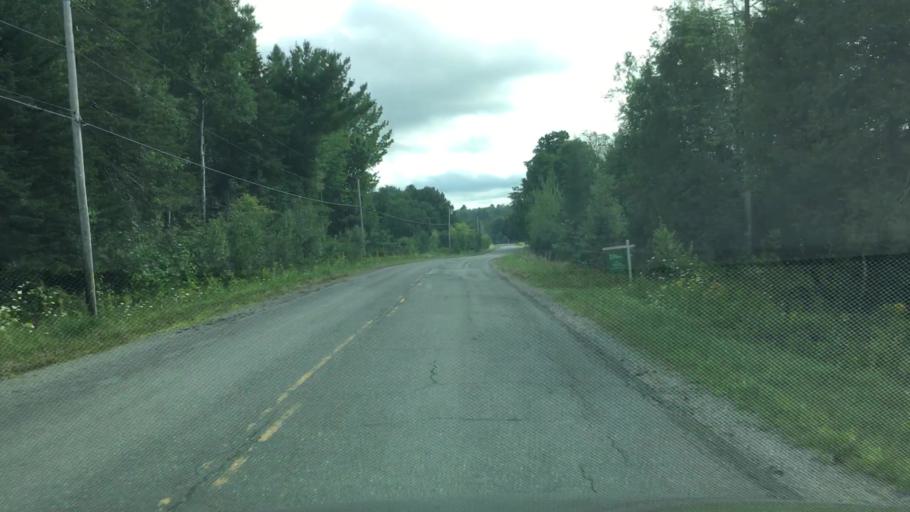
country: US
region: Maine
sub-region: Penobscot County
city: Hampden
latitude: 44.7212
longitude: -68.8666
